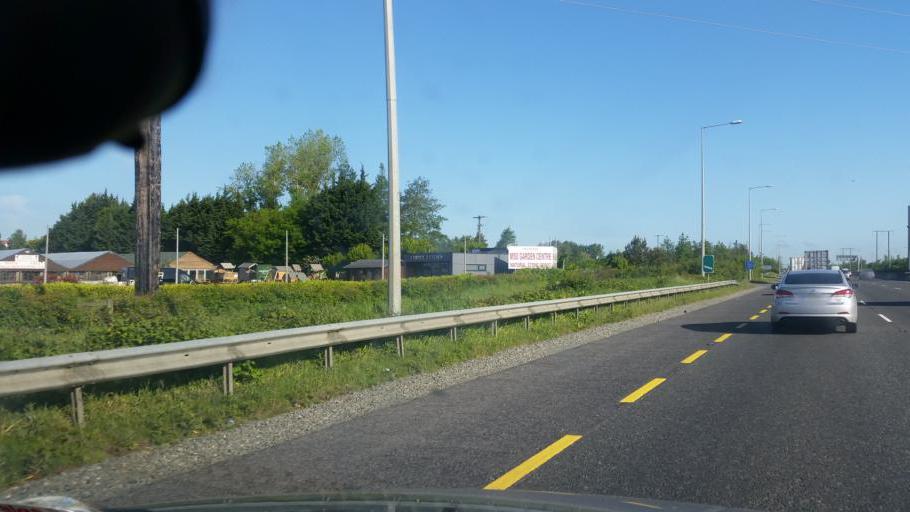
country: IE
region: Leinster
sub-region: Dublin City
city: Finglas
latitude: 53.4110
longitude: -6.3146
